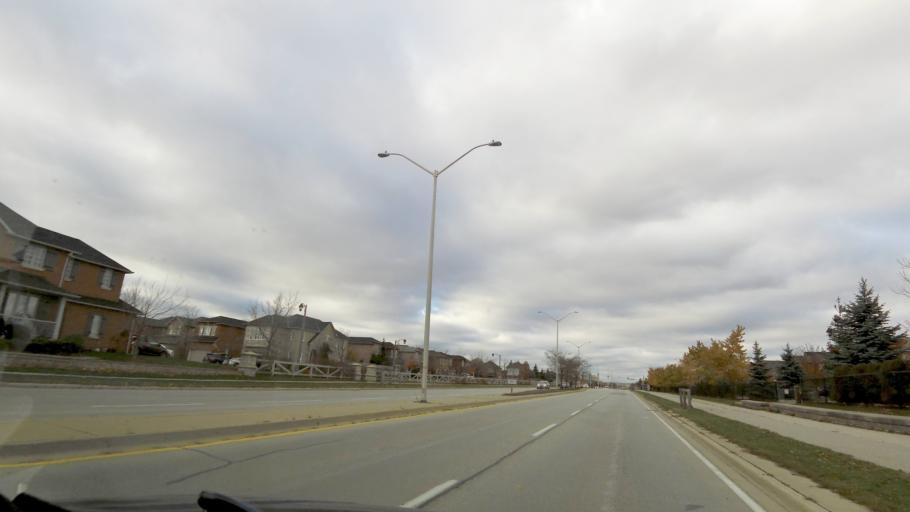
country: CA
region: Ontario
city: Oakville
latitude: 43.4400
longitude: -79.7465
